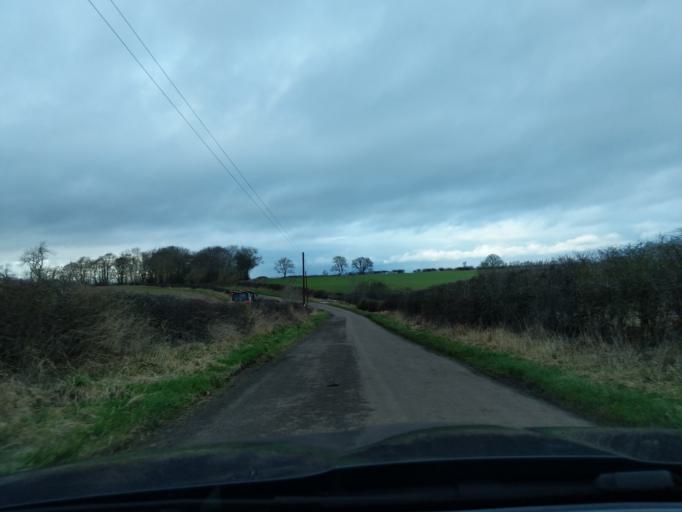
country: GB
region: England
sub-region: Northumberland
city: Ancroft
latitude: 55.7081
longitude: -2.0293
